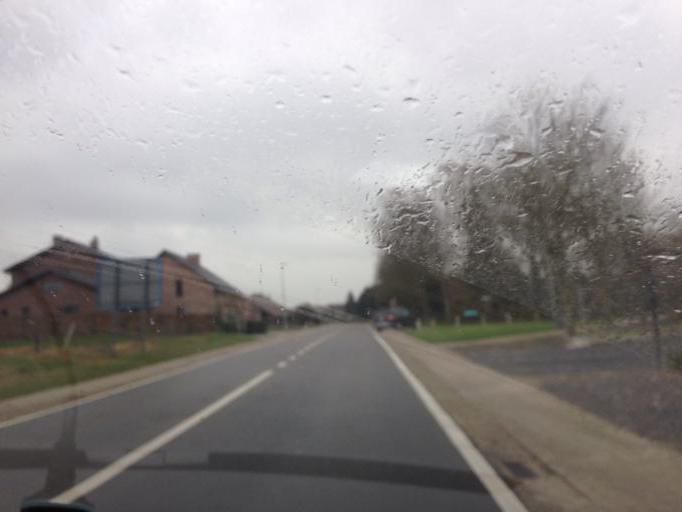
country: BE
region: Flanders
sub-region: Provincie Limburg
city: Opglabbeek
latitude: 51.0701
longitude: 5.5252
